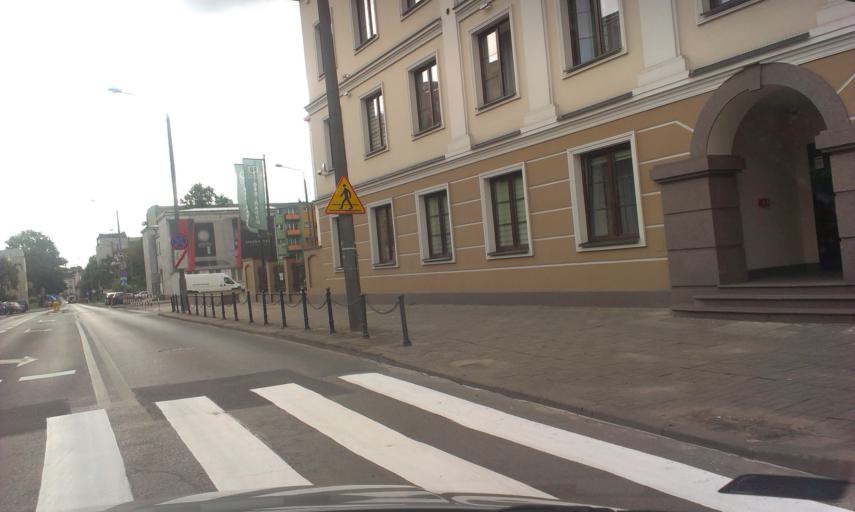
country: PL
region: Masovian Voivodeship
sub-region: Radom
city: Radom
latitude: 51.3952
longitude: 21.1549
